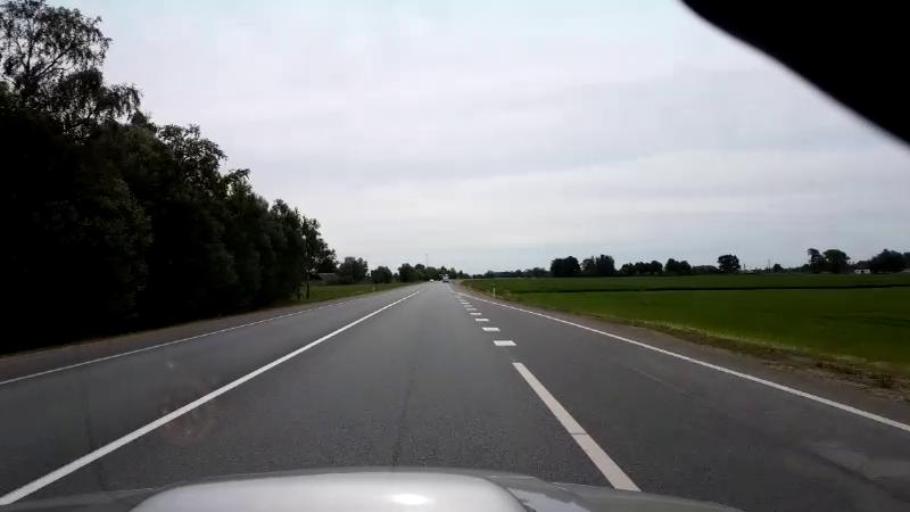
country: LV
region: Bauskas Rajons
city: Bauska
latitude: 56.4360
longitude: 24.1758
